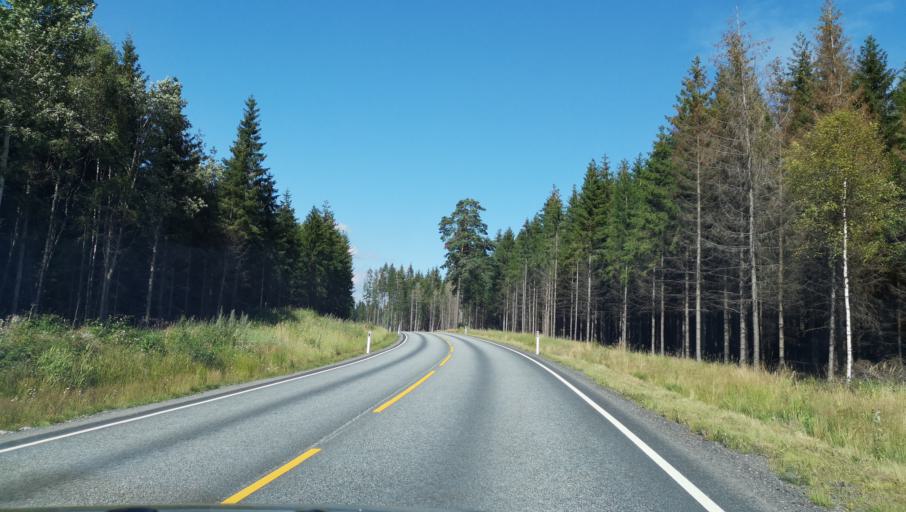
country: NO
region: Ostfold
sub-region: Valer
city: Kirkebygda
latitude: 59.5756
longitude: 10.8745
